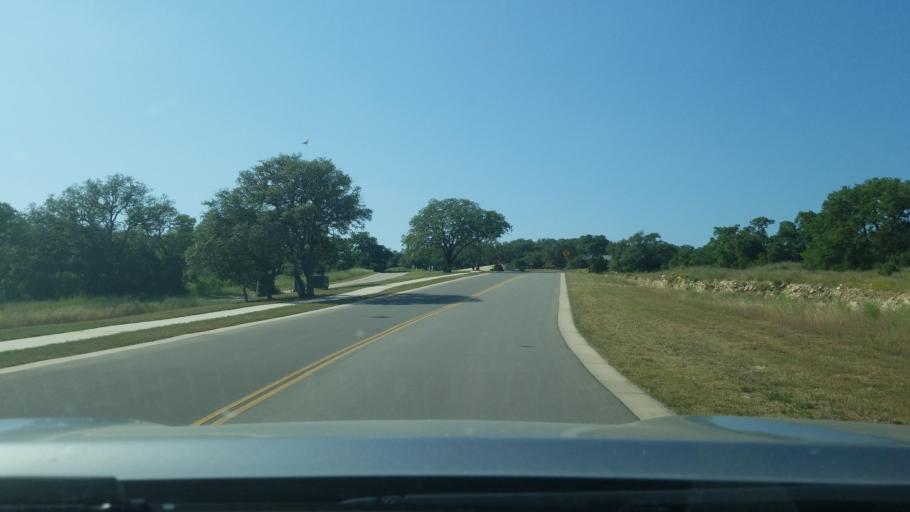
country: US
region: Texas
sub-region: Comal County
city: Bulverde
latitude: 29.7598
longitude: -98.4219
